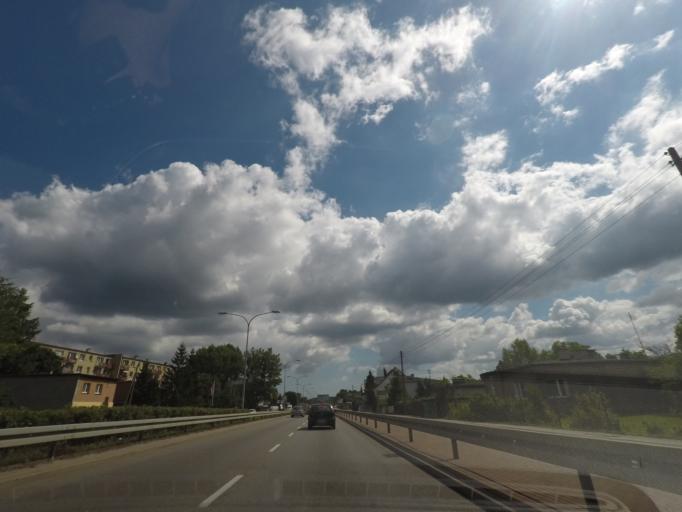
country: PL
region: Pomeranian Voivodeship
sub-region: Powiat wejherowski
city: Wejherowo
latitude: 54.6037
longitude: 18.2547
